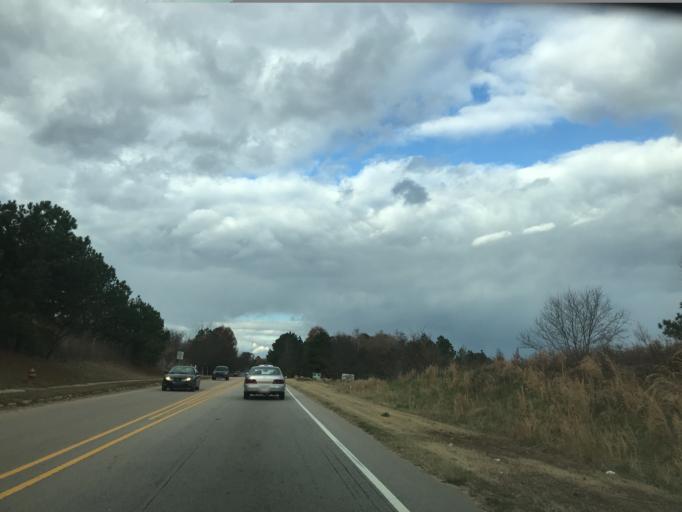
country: US
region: North Carolina
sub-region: Wake County
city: Raleigh
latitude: 35.7857
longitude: -78.5605
